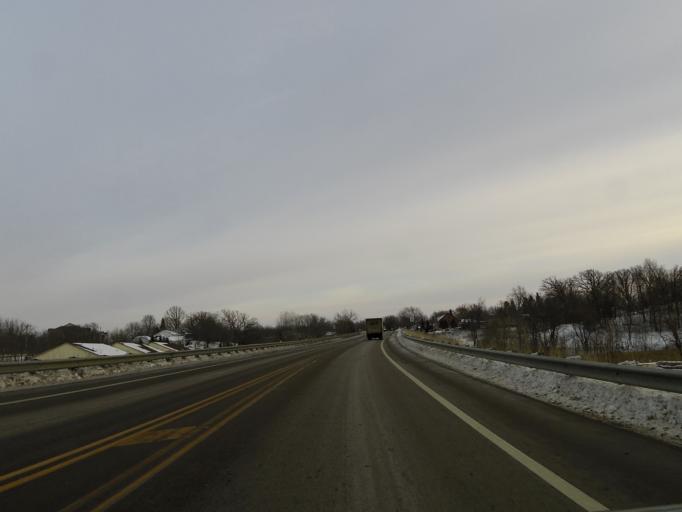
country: US
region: Minnesota
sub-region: Carver County
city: Victoria
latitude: 44.8608
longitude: -93.6680
